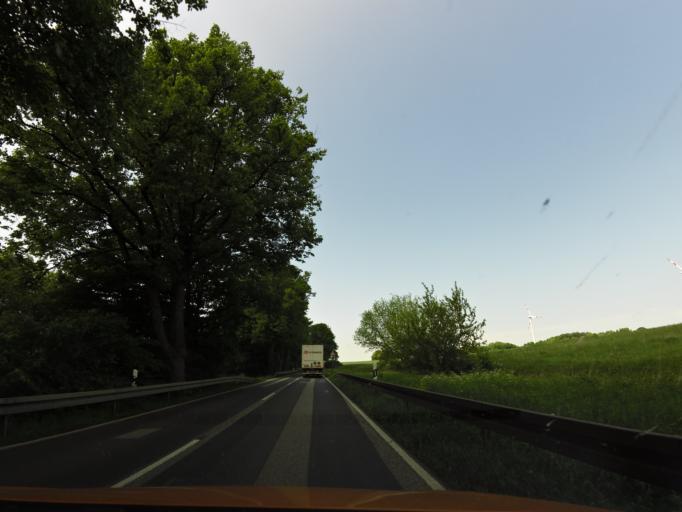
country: DE
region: Mecklenburg-Vorpommern
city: Selmsdorf
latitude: 53.8697
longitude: 10.8942
